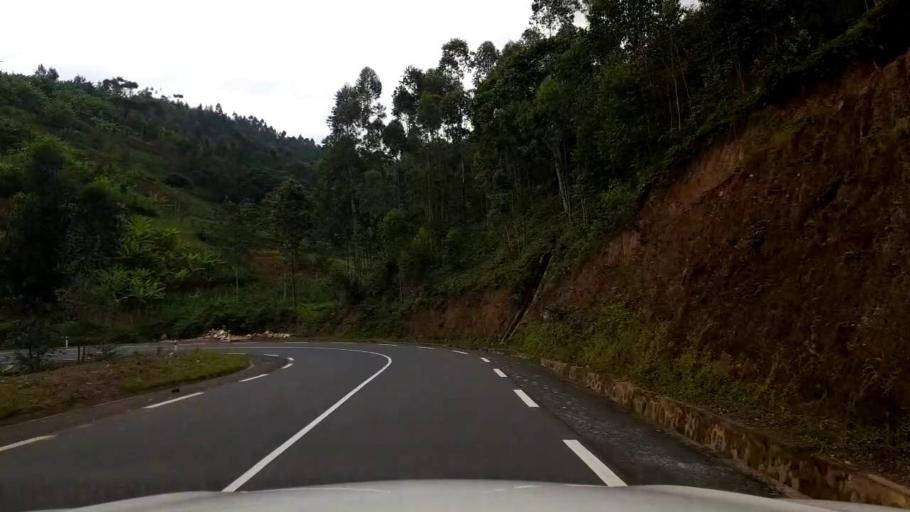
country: RW
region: Western Province
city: Kibuye
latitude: -1.9064
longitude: 29.3617
